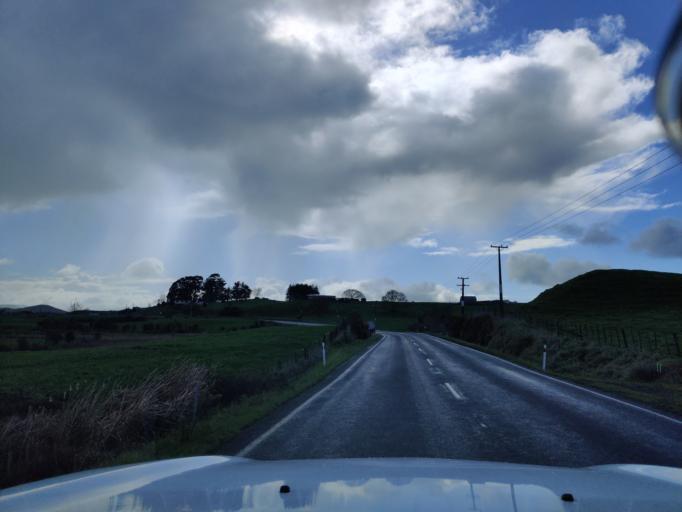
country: NZ
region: Waikato
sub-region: Waikato District
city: Ngaruawahia
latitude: -37.5895
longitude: 175.2126
